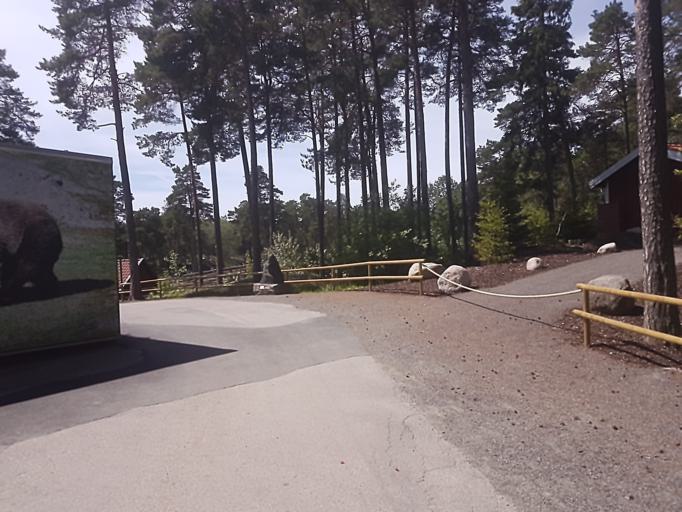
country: SE
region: OEstergoetland
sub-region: Norrkopings Kommun
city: Krokek
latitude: 58.6623
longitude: 16.4617
